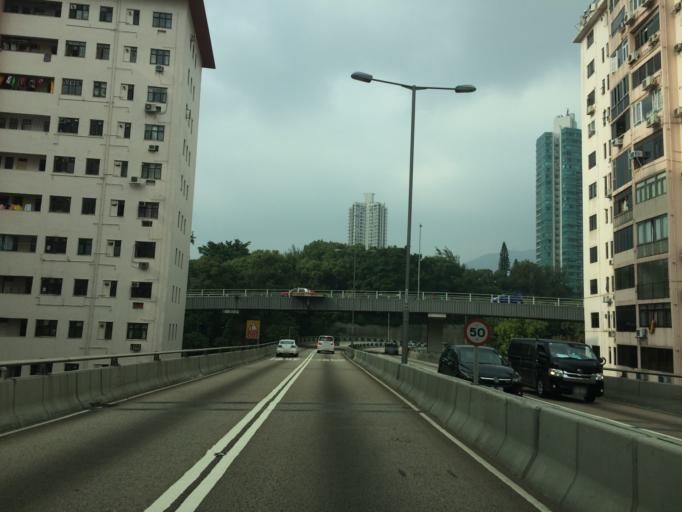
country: HK
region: Kowloon City
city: Kowloon
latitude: 22.3208
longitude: 114.1786
